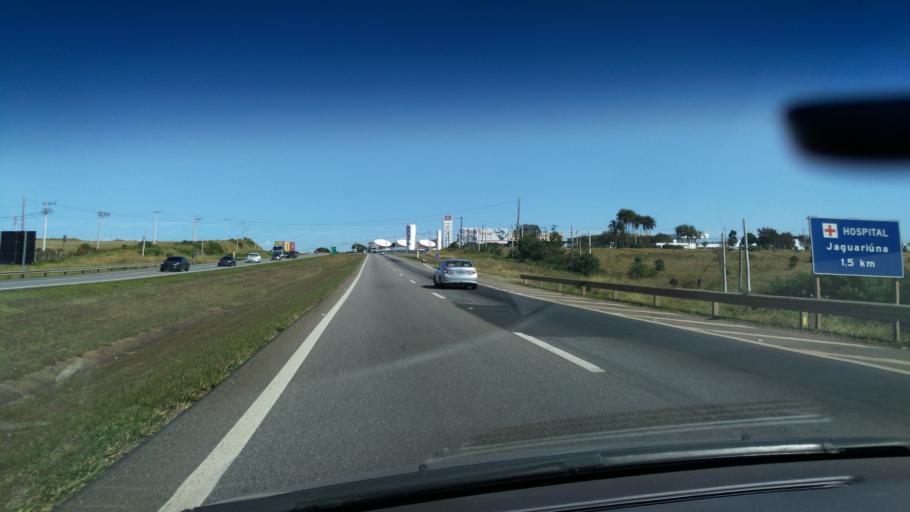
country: BR
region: Sao Paulo
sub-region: Jaguariuna
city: Jaguariuna
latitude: -22.6853
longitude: -47.0098
